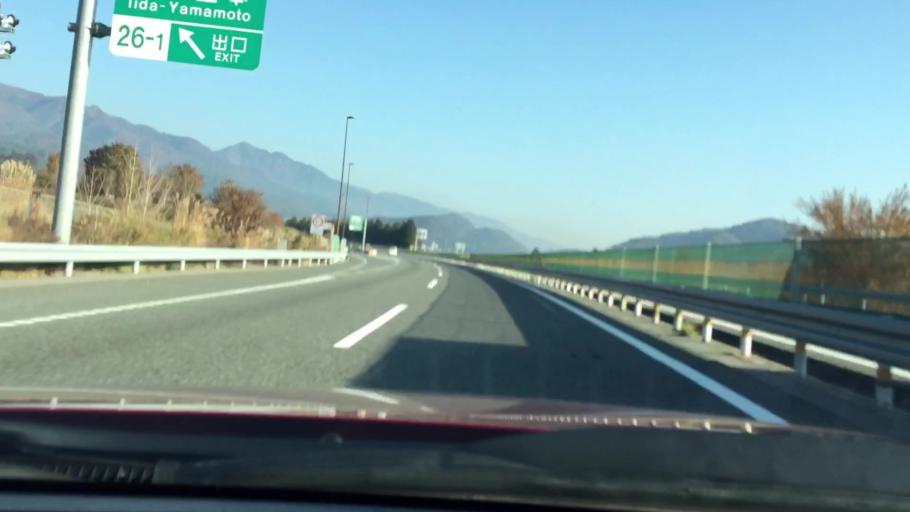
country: JP
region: Nagano
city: Iida
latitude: 35.4672
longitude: 137.7578
